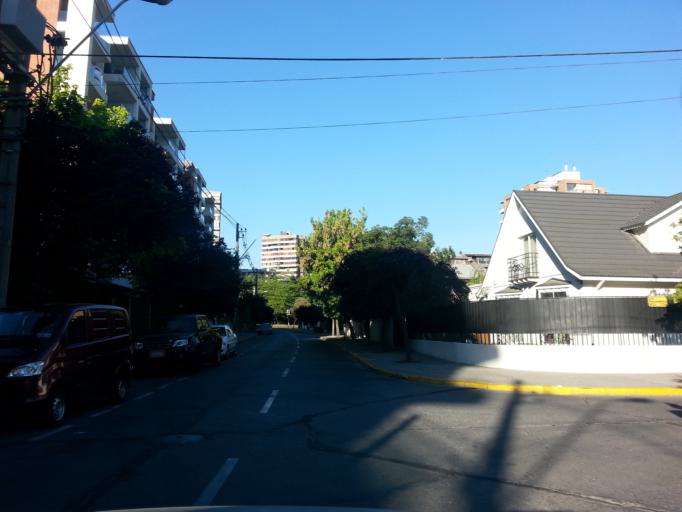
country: CL
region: Santiago Metropolitan
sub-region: Provincia de Santiago
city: Villa Presidente Frei, Nunoa, Santiago, Chile
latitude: -33.4290
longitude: -70.5901
